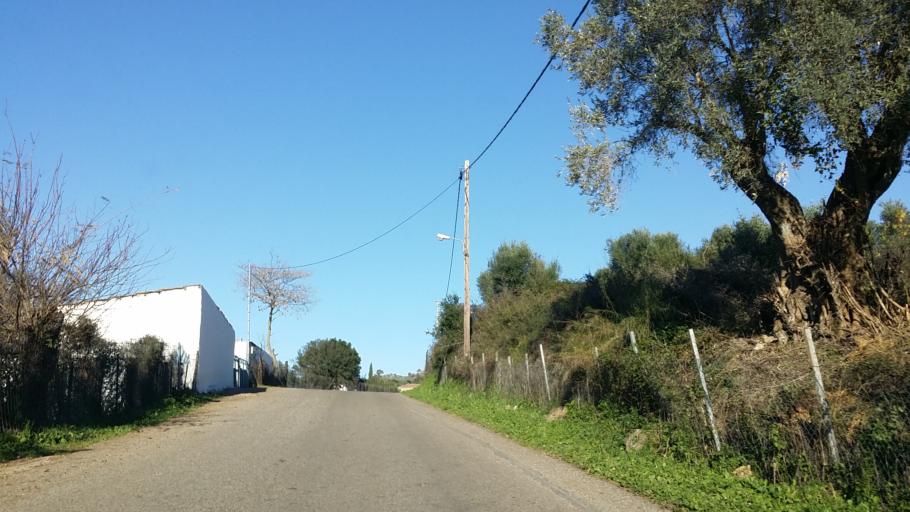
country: GR
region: West Greece
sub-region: Nomos Aitolias kai Akarnanias
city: Fitiai
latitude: 38.6402
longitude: 21.1775
